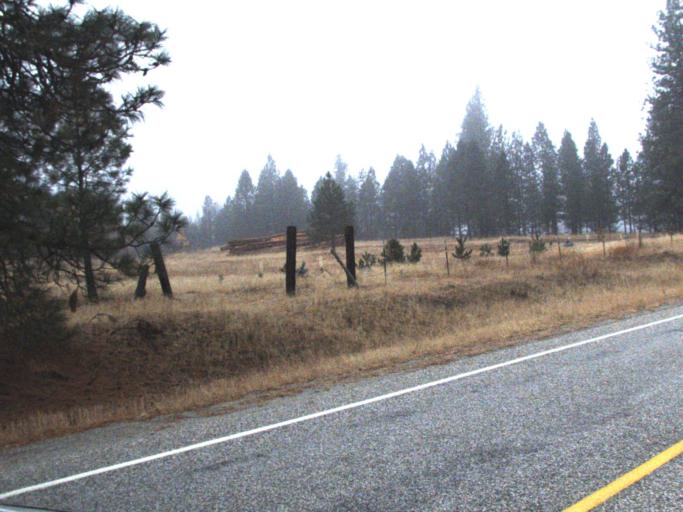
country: US
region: Washington
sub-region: Stevens County
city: Kettle Falls
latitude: 48.7223
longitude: -118.1318
